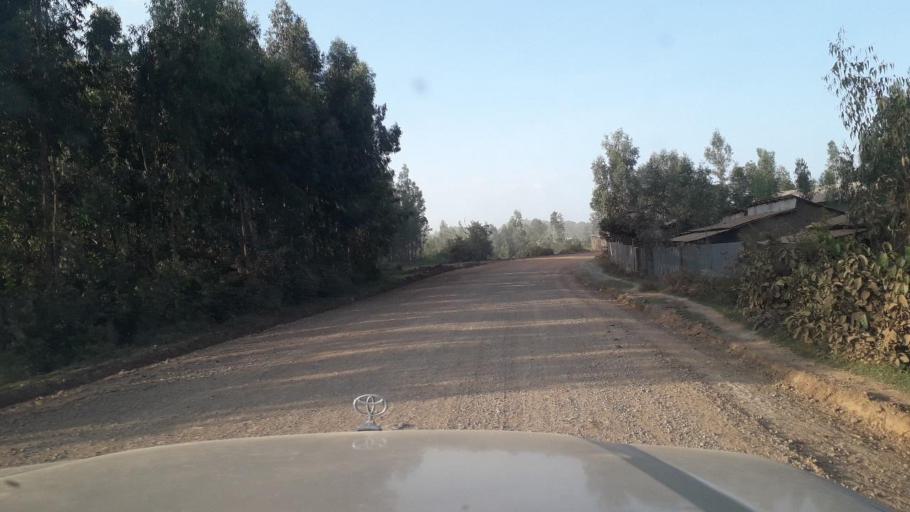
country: ET
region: Oromiya
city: Jima
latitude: 7.6178
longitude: 36.8342
